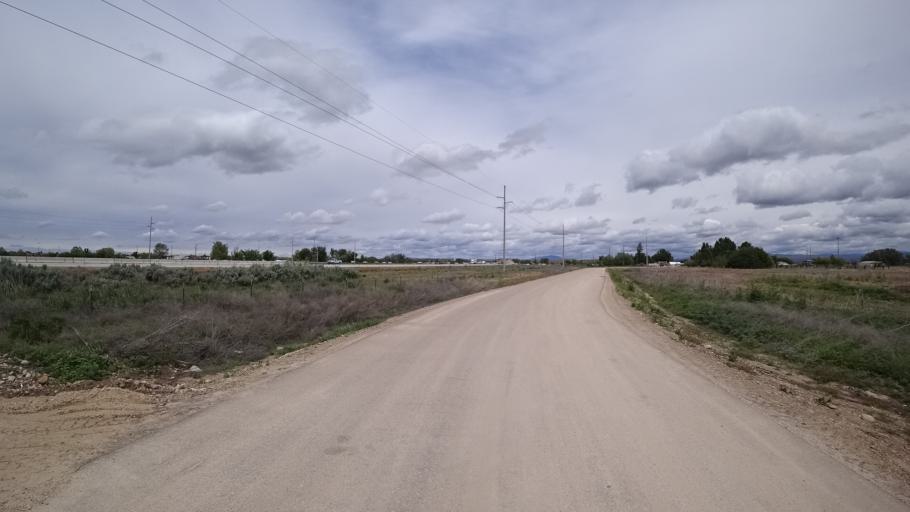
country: US
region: Idaho
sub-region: Ada County
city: Star
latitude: 43.6879
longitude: -116.4599
